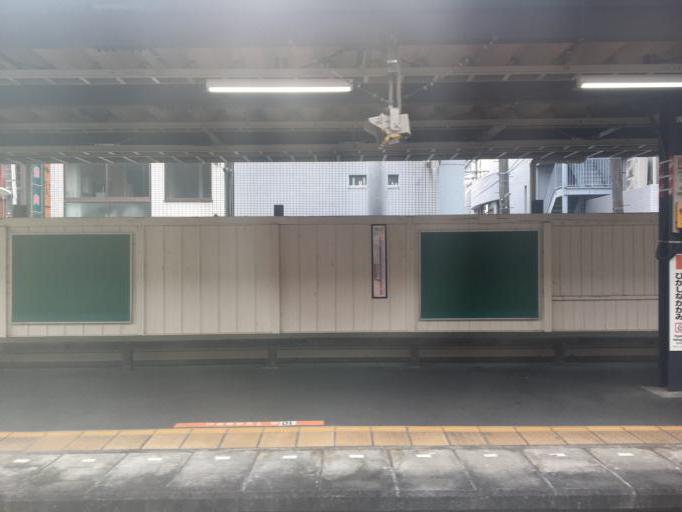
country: JP
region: Tokyo
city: Hino
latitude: 35.7063
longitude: 139.3847
